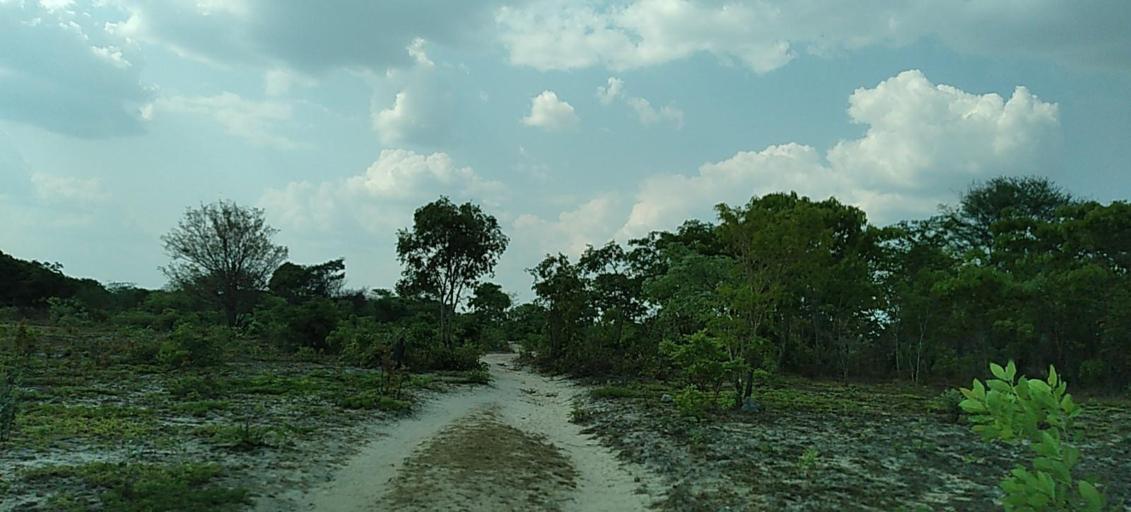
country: ZM
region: Copperbelt
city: Luanshya
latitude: -13.2195
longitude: 28.3314
